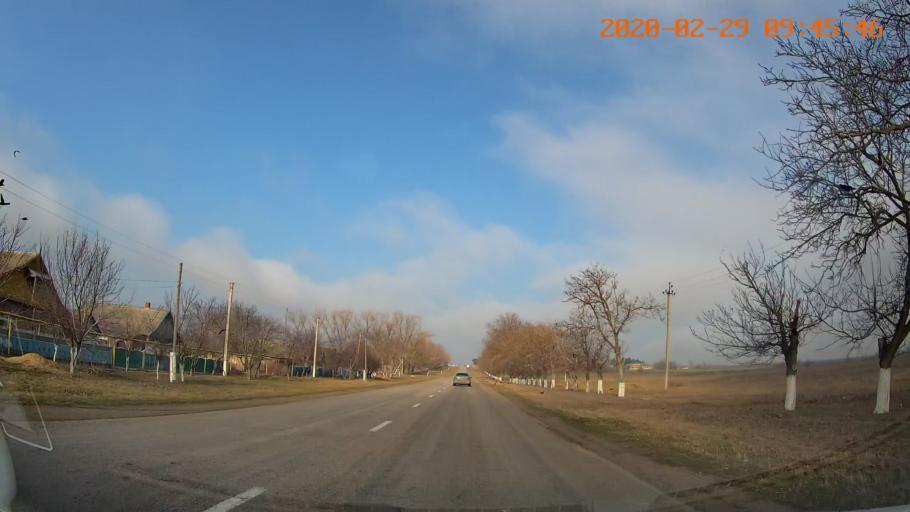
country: MD
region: Telenesti
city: Crasnoe
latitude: 46.6617
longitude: 29.8065
